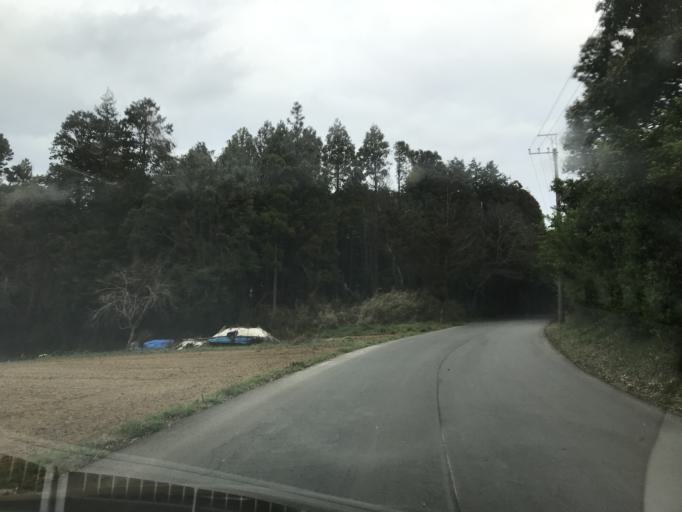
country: JP
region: Chiba
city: Sawara
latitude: 35.8540
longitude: 140.4778
